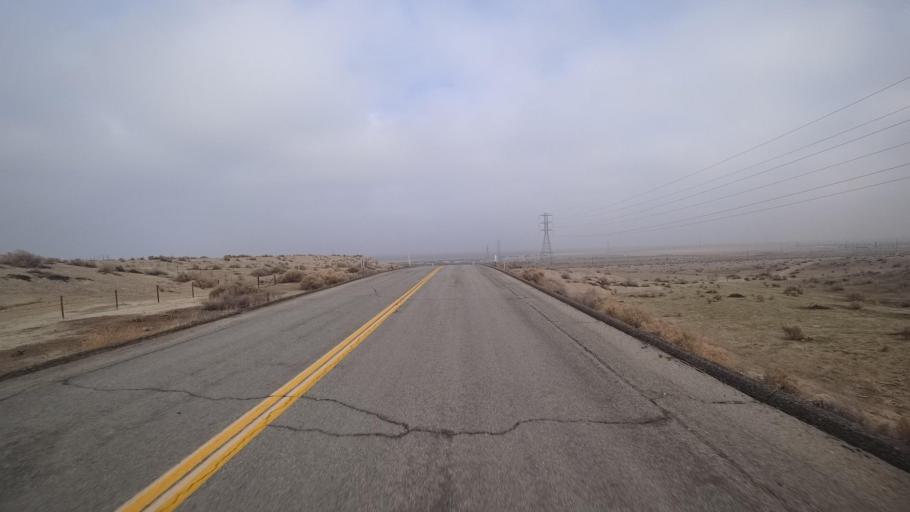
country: US
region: California
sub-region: Kern County
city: Ford City
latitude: 35.1590
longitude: -119.3413
